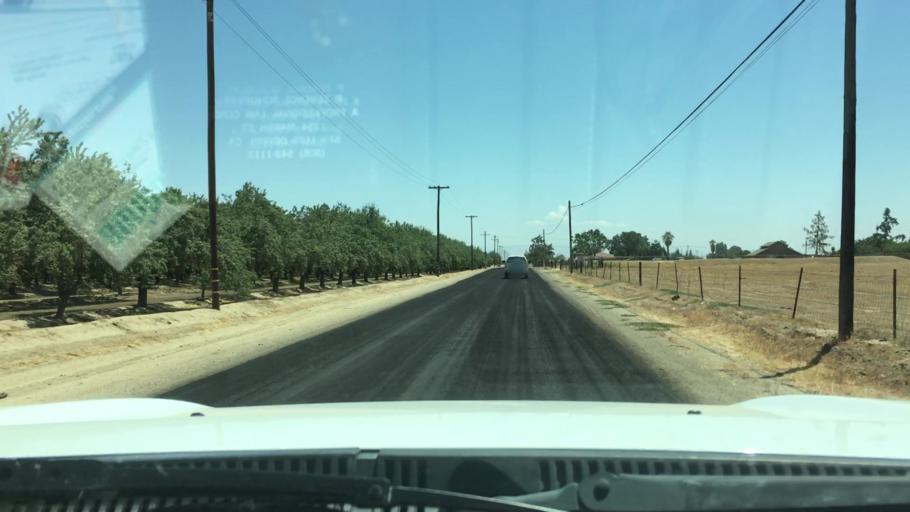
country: US
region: California
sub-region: Kern County
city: Shafter
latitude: 35.5291
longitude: -119.3172
